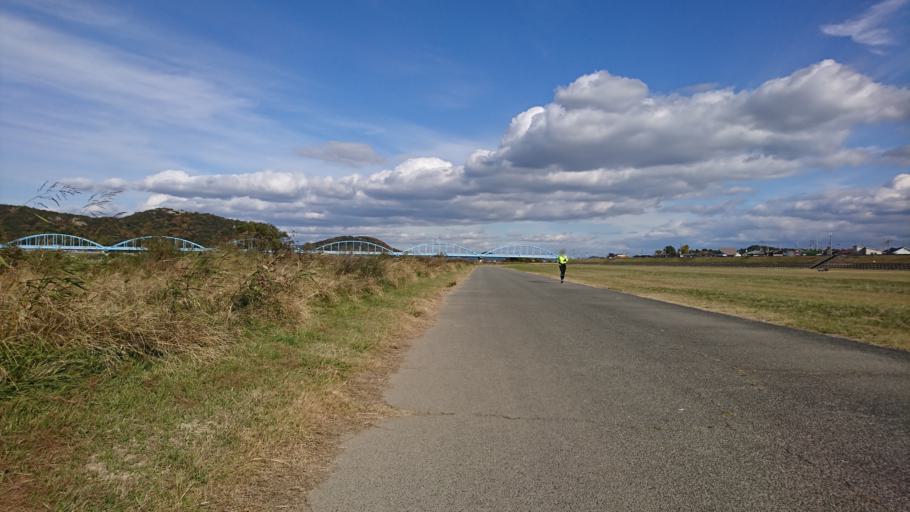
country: JP
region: Hyogo
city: Kakogawacho-honmachi
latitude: 34.7781
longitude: 134.8435
